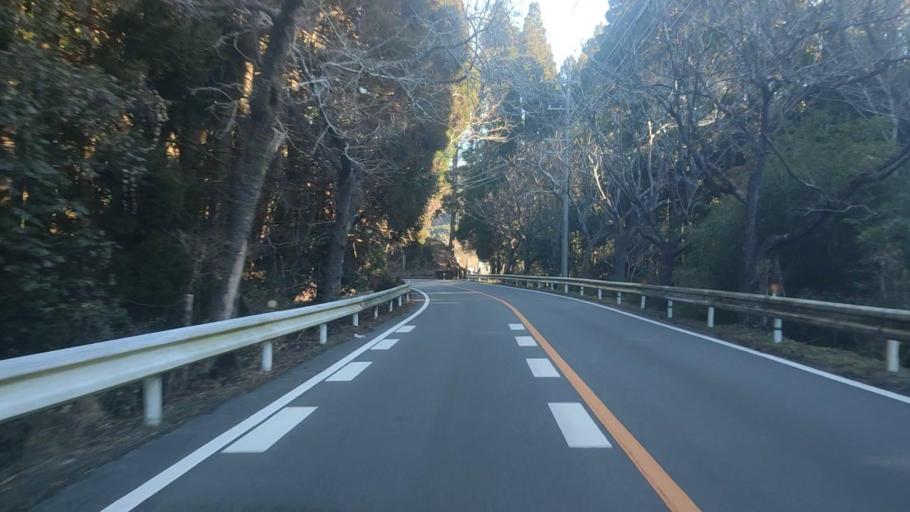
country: JP
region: Miyazaki
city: Nobeoka
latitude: 32.6398
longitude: 131.7437
